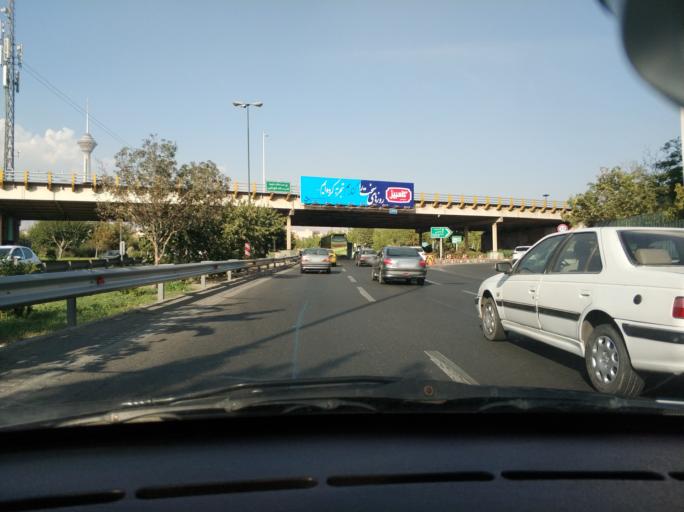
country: IR
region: Tehran
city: Tehran
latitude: 35.7284
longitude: 51.3683
